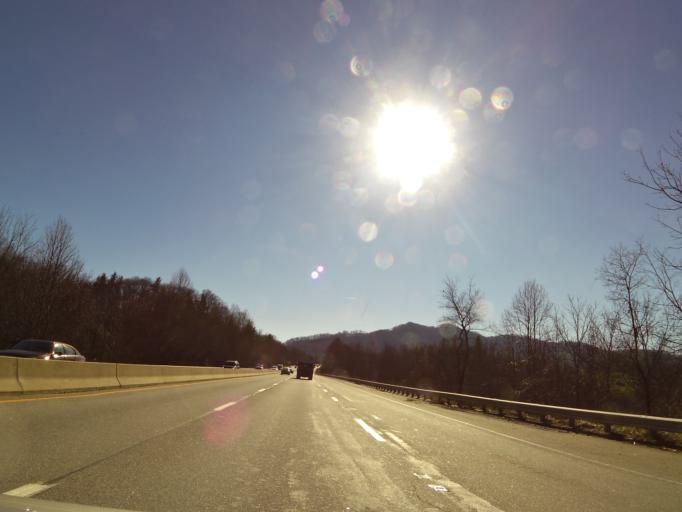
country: US
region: North Carolina
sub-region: Haywood County
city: Cove Creek
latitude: 35.5982
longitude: -83.0038
